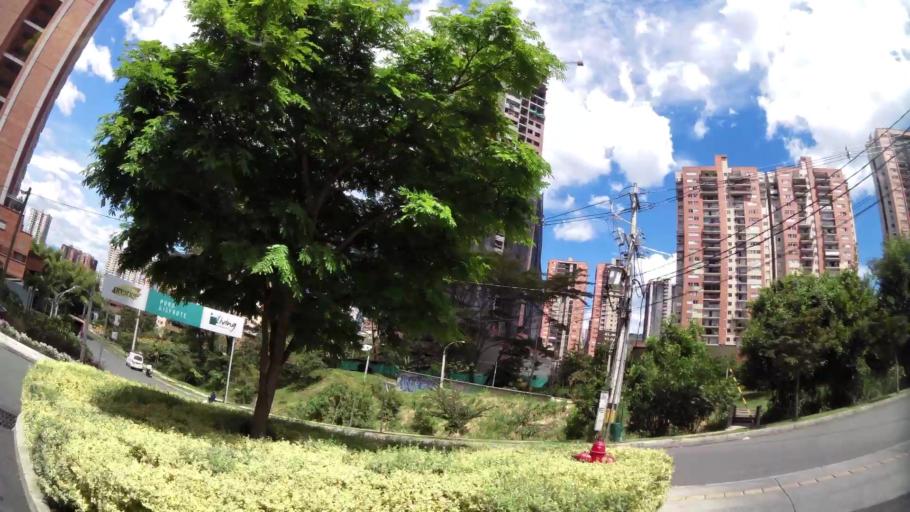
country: CO
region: Antioquia
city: Sabaneta
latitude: 6.1437
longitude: -75.6225
